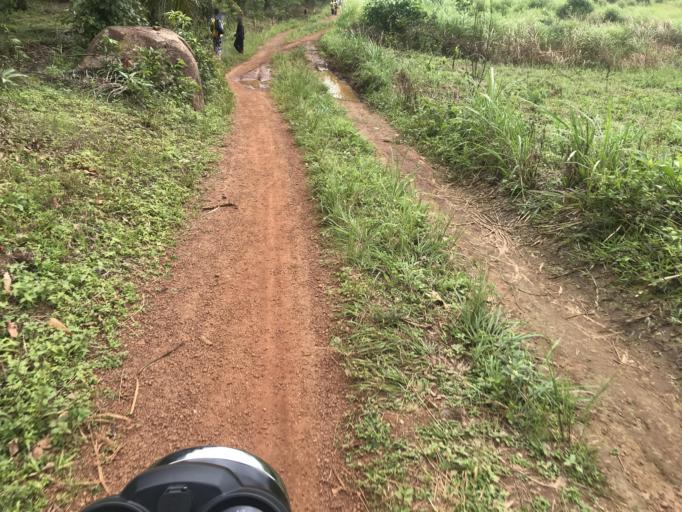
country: SL
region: Eastern Province
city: Buedu
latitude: 8.4697
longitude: -10.3301
